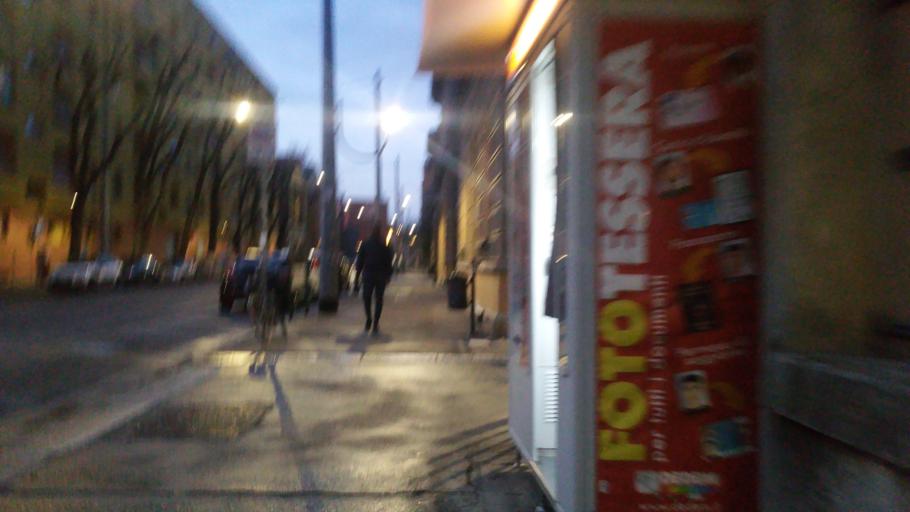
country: IT
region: Emilia-Romagna
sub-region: Provincia di Bologna
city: Bologna
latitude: 44.5022
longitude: 11.3277
